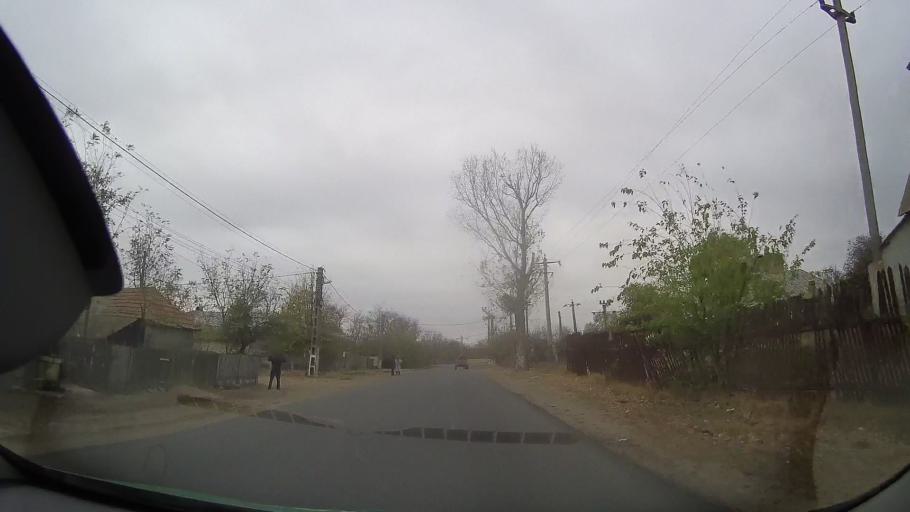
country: RO
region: Braila
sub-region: Comuna Ciresu
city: Ciresu
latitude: 44.9394
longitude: 27.3692
